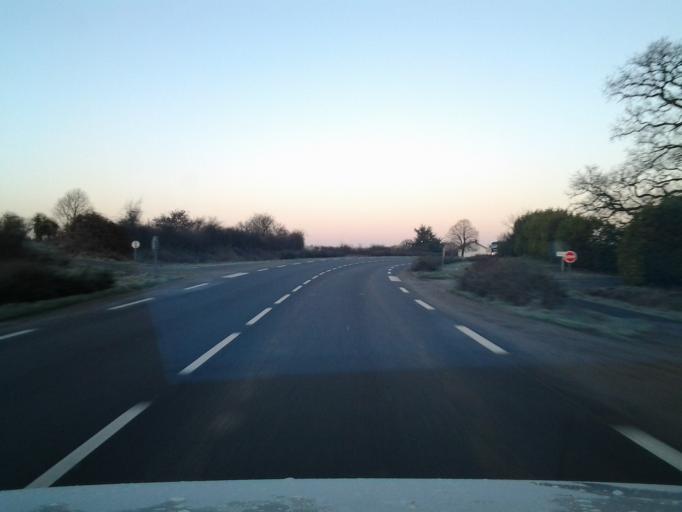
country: FR
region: Pays de la Loire
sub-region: Departement de la Vendee
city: Chambretaud
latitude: 46.9276
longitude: -0.9814
